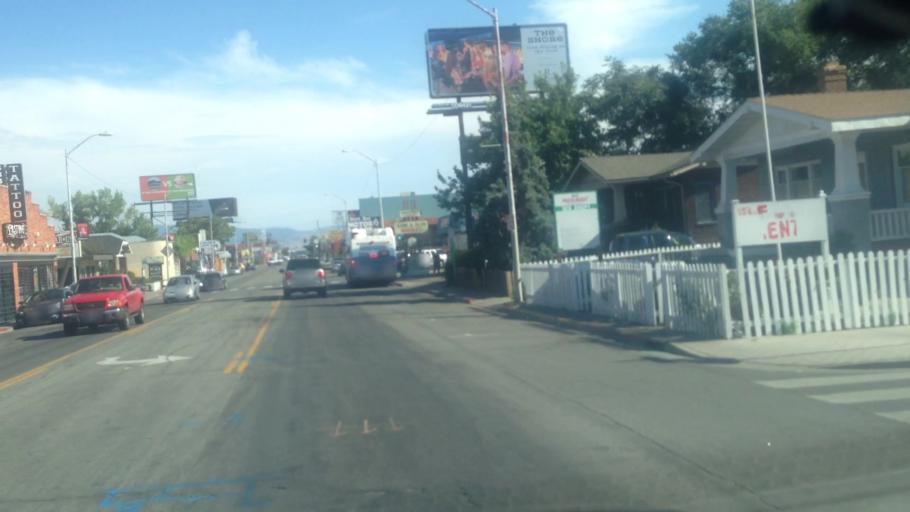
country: US
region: Nevada
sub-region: Washoe County
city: Reno
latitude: 39.5170
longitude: -119.8087
